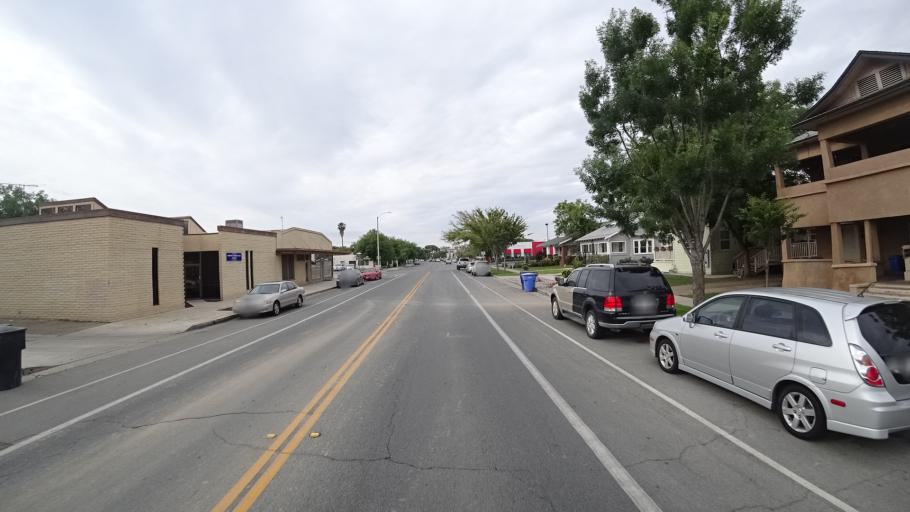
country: US
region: California
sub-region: Kings County
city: Hanford
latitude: 36.3296
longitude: -119.6496
